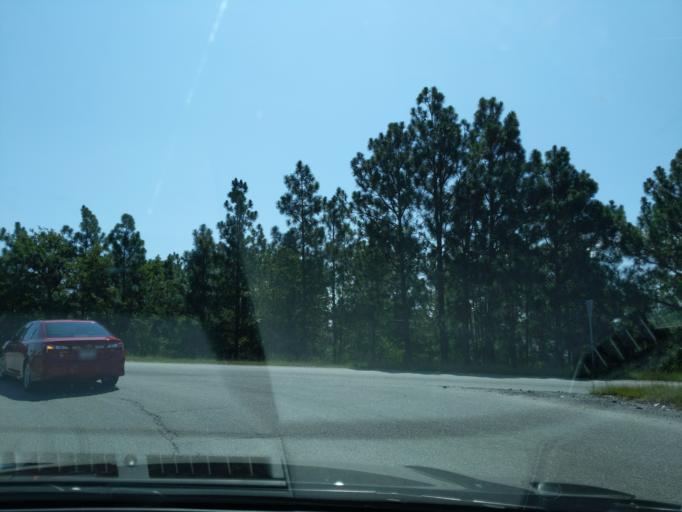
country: US
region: South Carolina
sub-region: Lexington County
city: Red Bank
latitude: 33.9253
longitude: -81.2897
